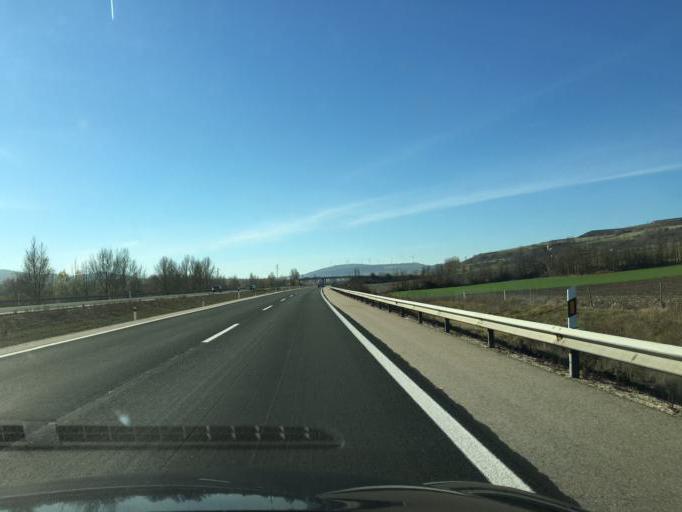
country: ES
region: Castille and Leon
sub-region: Provincia de Burgos
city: Castil de Peones
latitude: 42.4869
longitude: -3.3885
